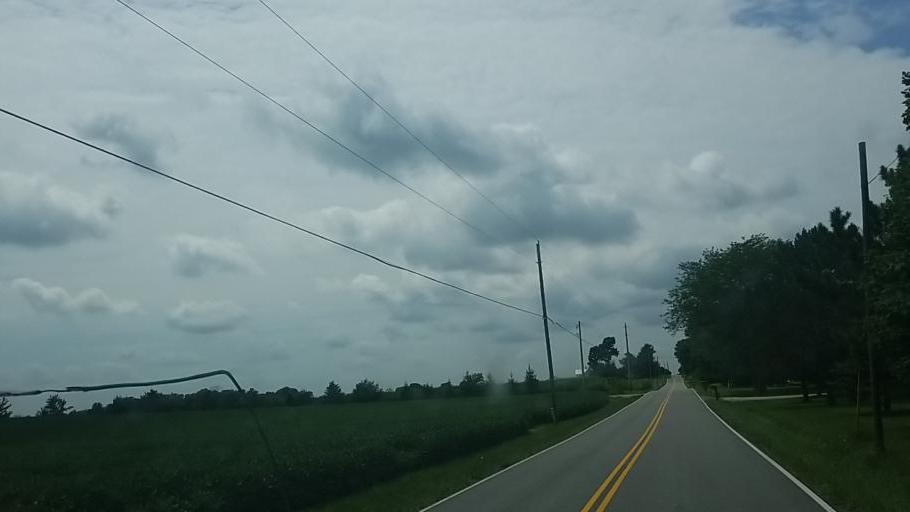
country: US
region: Ohio
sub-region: Fairfield County
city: Lithopolis
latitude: 39.7502
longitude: -82.8049
